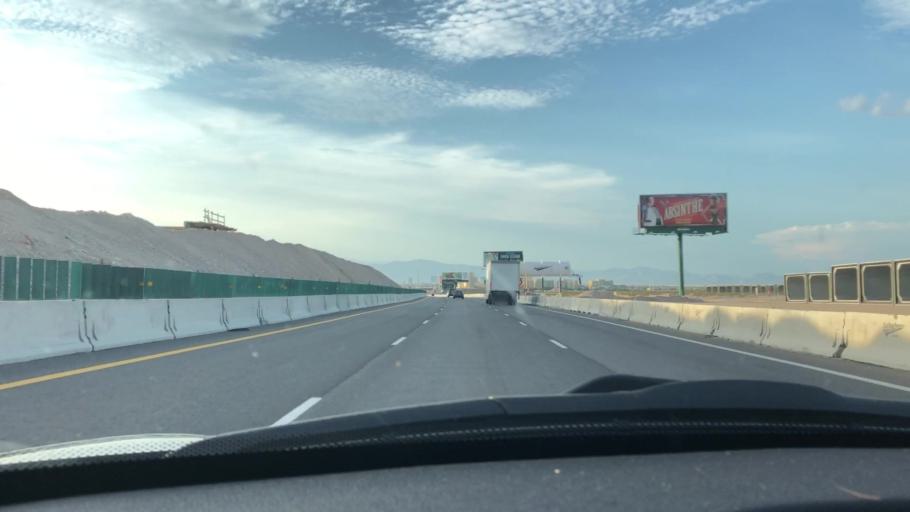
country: US
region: Nevada
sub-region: Clark County
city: Enterprise
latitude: 35.9833
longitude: -115.1804
